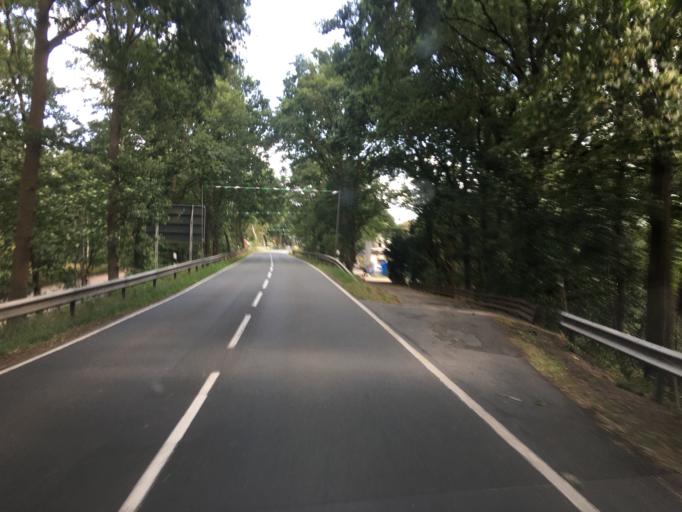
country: DE
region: Lower Saxony
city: Friesoythe
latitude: 53.0827
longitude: 7.8341
